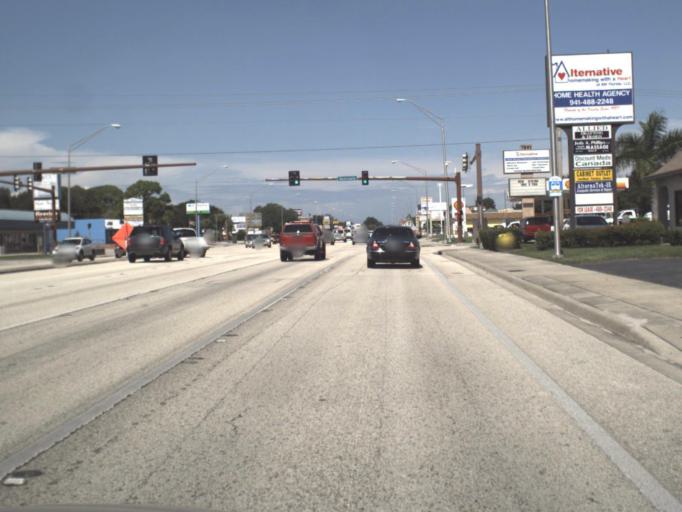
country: US
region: Florida
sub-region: Sarasota County
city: South Venice
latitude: 27.0616
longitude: -82.4159
